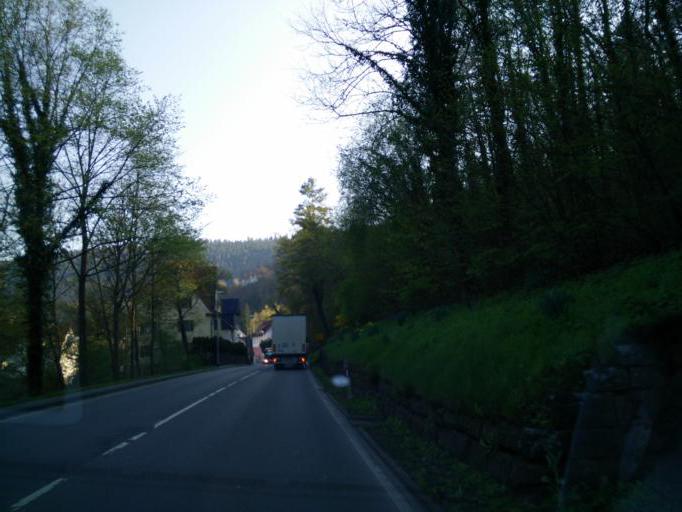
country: DE
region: Baden-Wuerttemberg
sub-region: Karlsruhe Region
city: Calw
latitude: 48.7323
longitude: 8.7349
